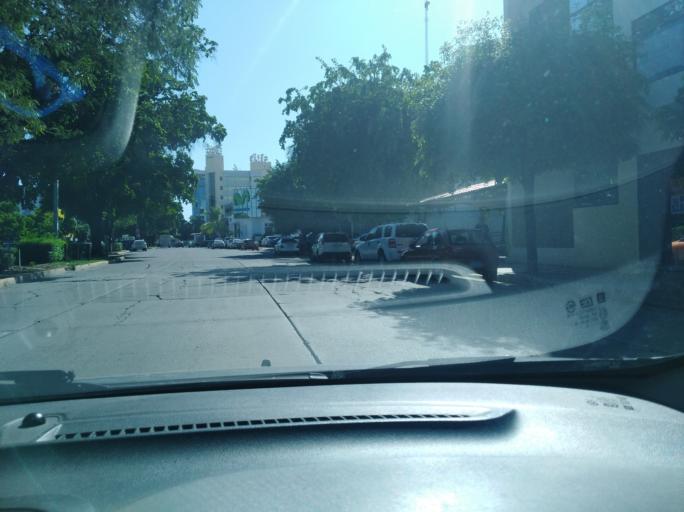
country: MX
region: Sinaloa
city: Culiacan
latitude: 24.7967
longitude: -107.4114
